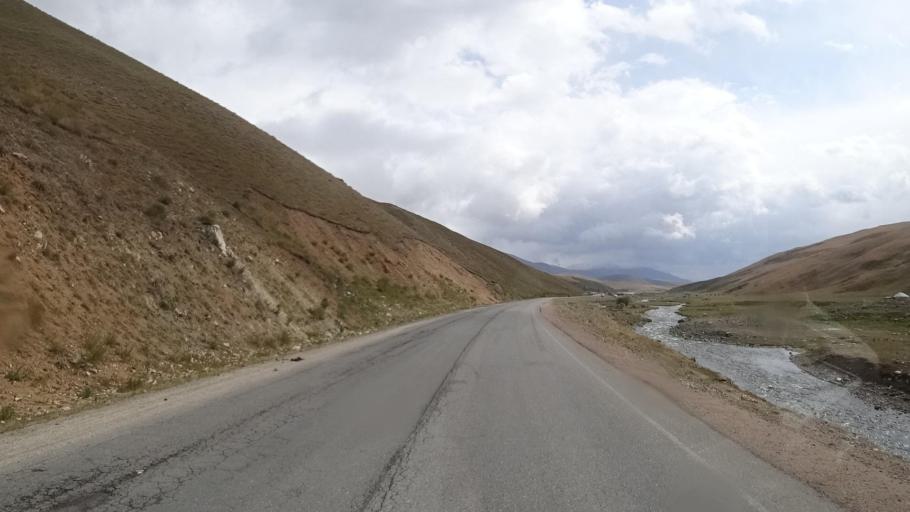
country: KG
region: Jalal-Abad
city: Uch-Terek
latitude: 42.2055
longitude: 73.2385
